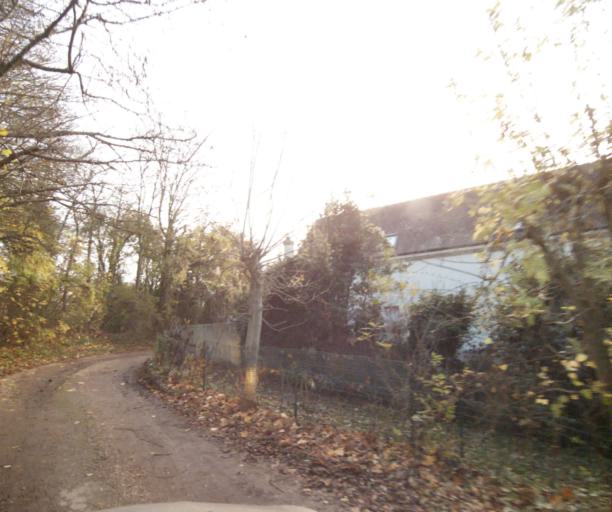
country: FR
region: Ile-de-France
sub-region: Departement des Yvelines
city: Triel-sur-Seine
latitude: 48.9857
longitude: 2.0082
